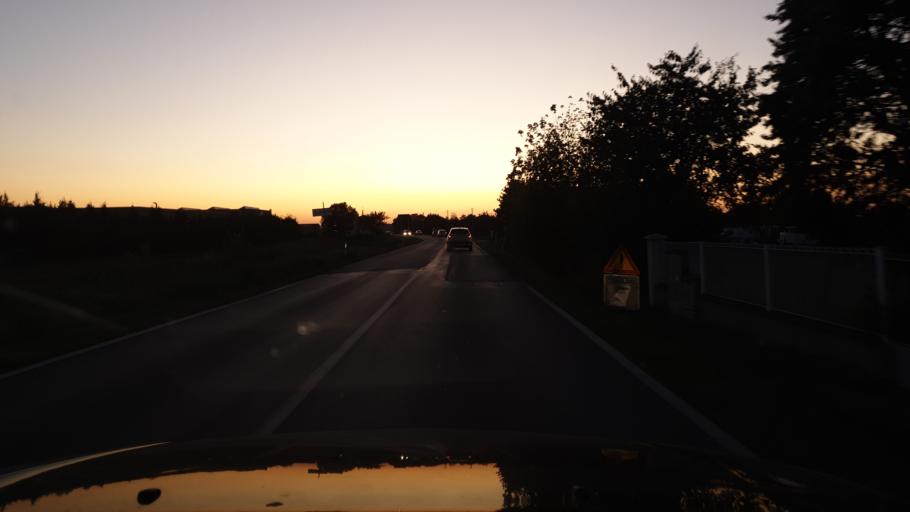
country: IT
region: Emilia-Romagna
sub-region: Provincia di Bologna
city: Altedo
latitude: 44.6838
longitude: 11.4898
